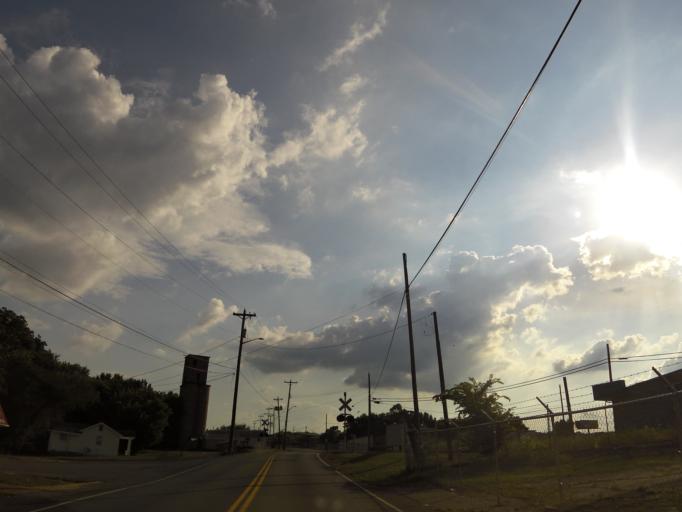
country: US
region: Tennessee
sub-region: Montgomery County
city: Clarksville
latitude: 36.5346
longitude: -87.3386
